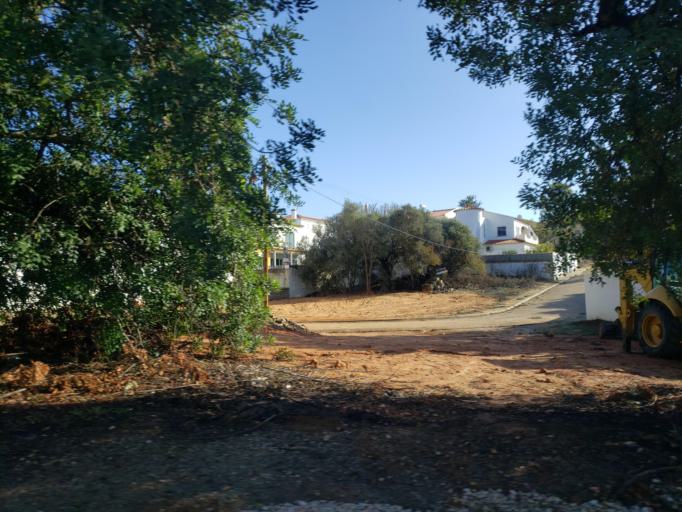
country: PT
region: Faro
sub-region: Portimao
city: Portimao
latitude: 37.1557
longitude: -8.5605
